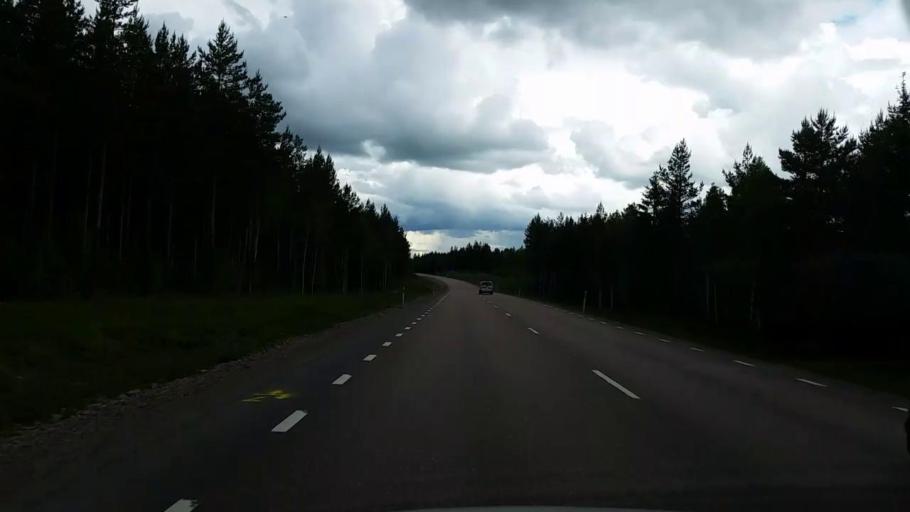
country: SE
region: Dalarna
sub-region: Avesta Kommun
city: Horndal
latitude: 60.4654
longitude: 16.4478
